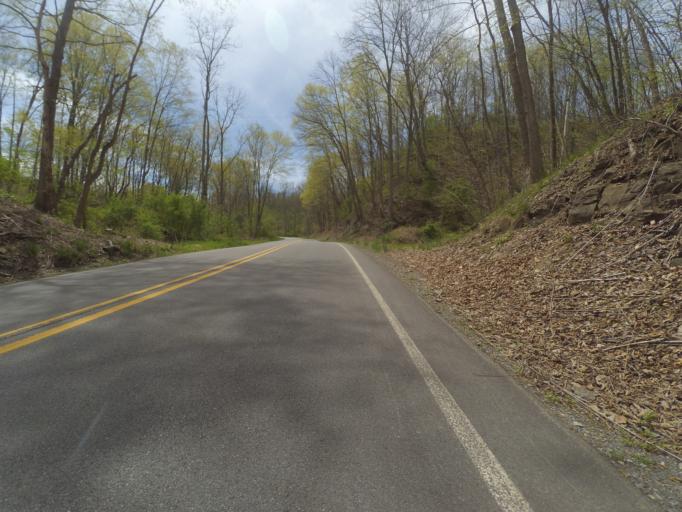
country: US
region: Pennsylvania
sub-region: Blair County
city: Tyrone
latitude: 40.6484
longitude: -78.2304
